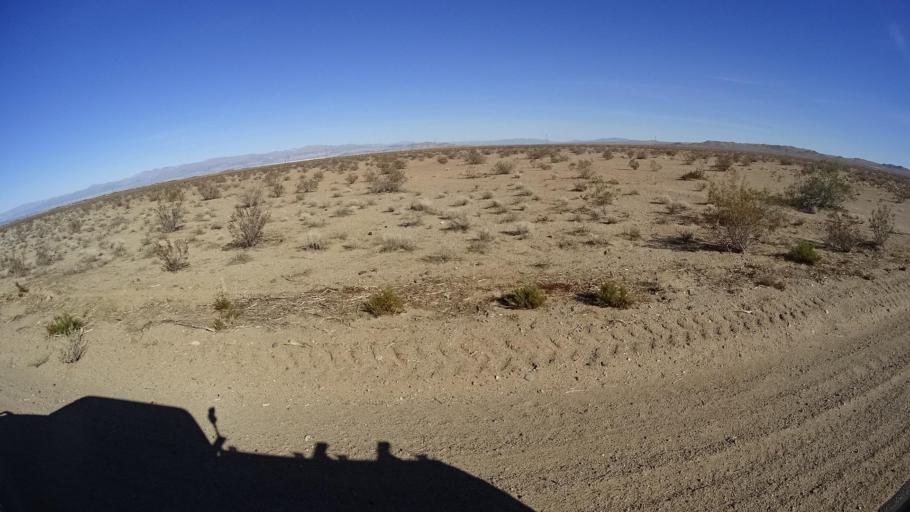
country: US
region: California
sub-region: Kern County
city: China Lake Acres
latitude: 35.5812
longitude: -117.7875
